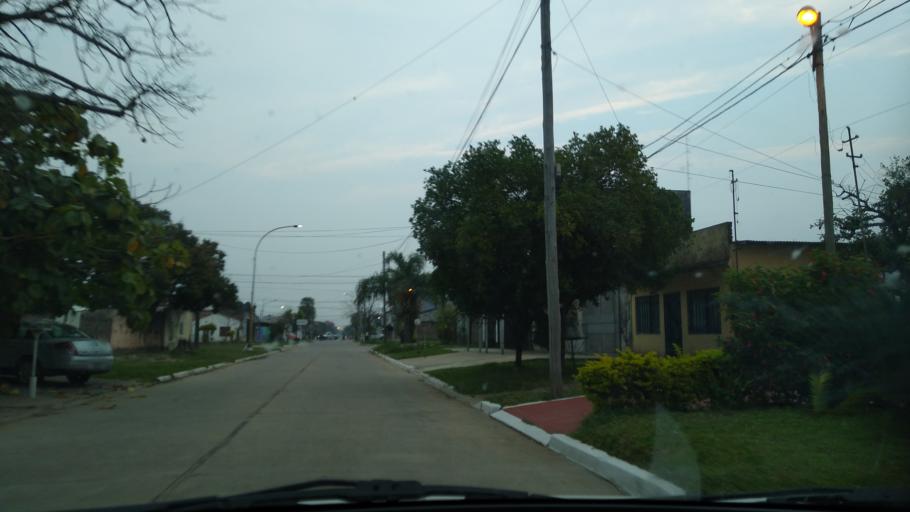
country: AR
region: Chaco
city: Barranqueras
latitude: -27.4820
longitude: -58.9455
